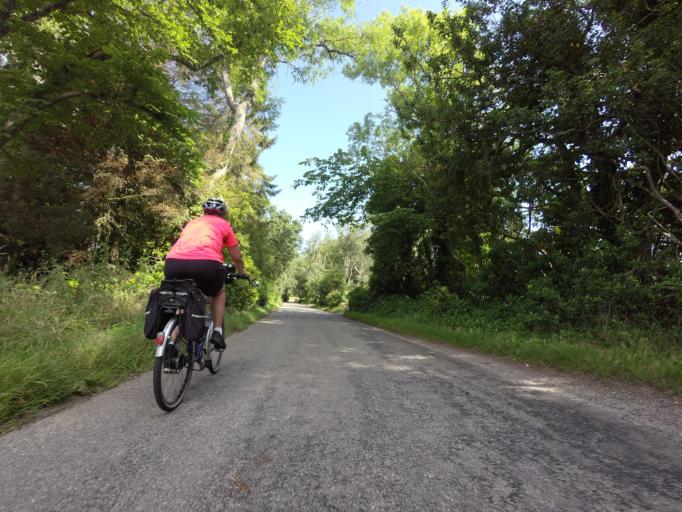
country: GB
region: Scotland
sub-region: Highland
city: Alness
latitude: 57.7157
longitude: -4.2171
